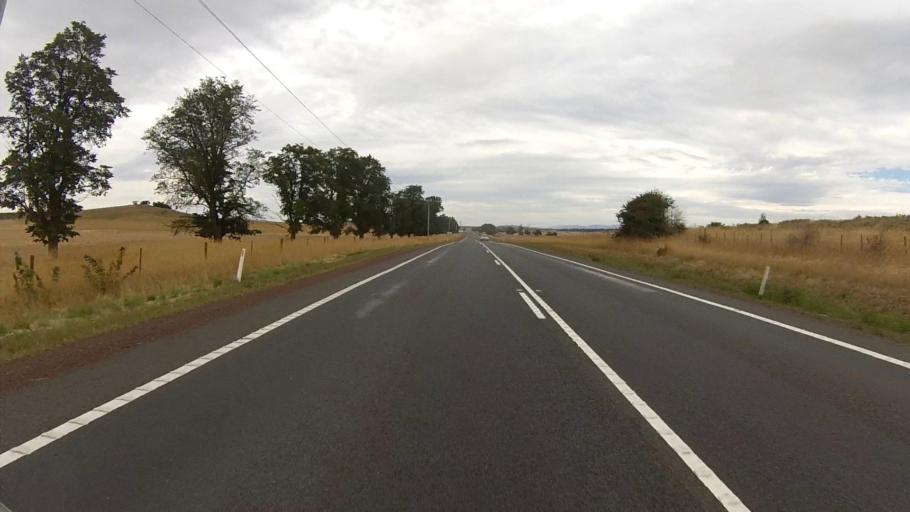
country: AU
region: Tasmania
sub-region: Northern Midlands
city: Evandale
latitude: -41.9052
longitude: 147.4786
